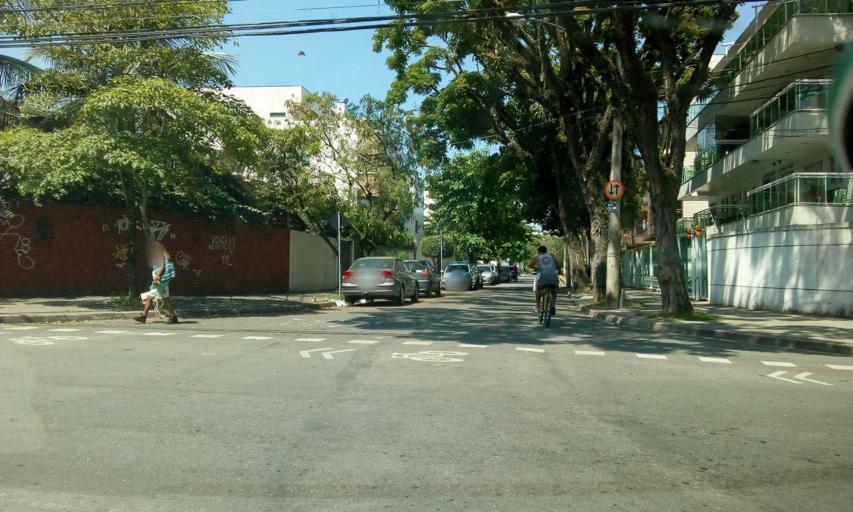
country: BR
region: Rio de Janeiro
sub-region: Nilopolis
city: Nilopolis
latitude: -23.0230
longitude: -43.4765
